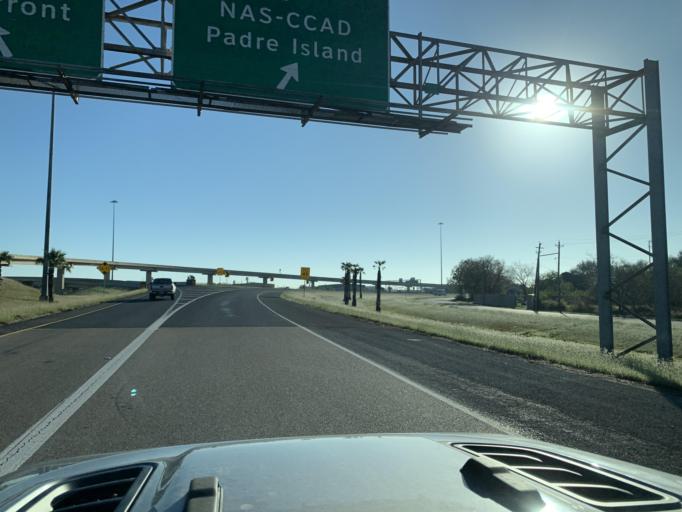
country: US
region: Texas
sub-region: Nueces County
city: Corpus Christi
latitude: 27.7817
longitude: -97.4723
